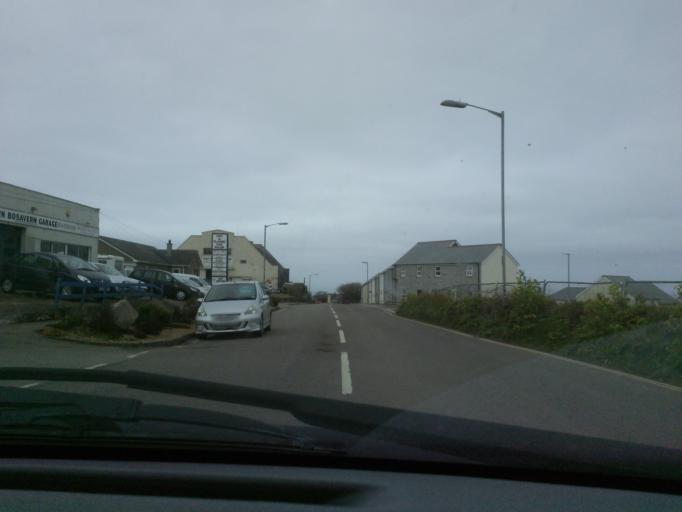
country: GB
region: England
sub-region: Cornwall
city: Saint Just
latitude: 50.1217
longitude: -5.6770
